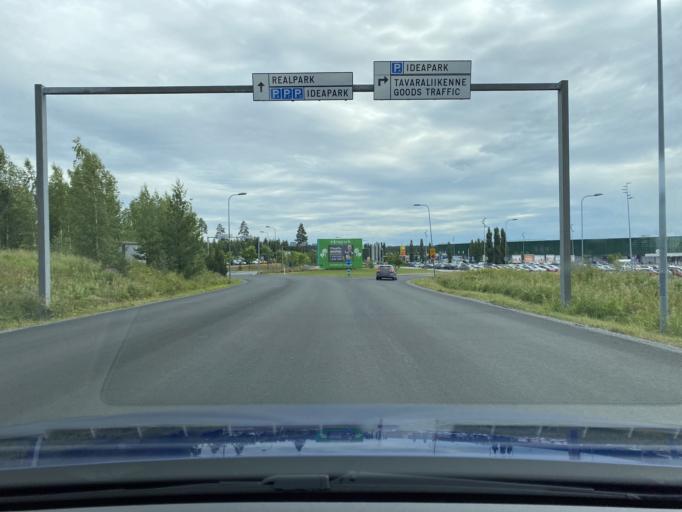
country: FI
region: Pirkanmaa
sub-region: Tampere
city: Lempaeaelae
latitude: 61.3654
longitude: 23.7984
